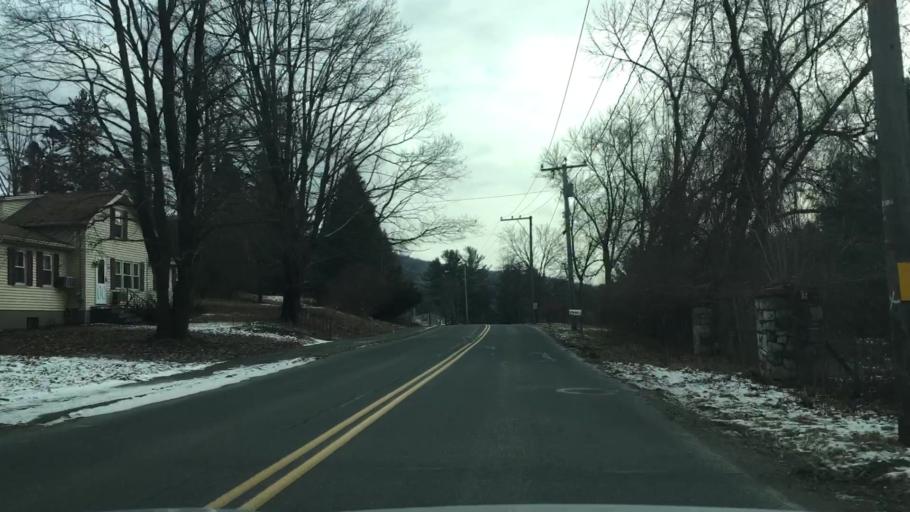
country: US
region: Massachusetts
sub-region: Berkshire County
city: Lee
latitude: 42.2942
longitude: -73.2467
